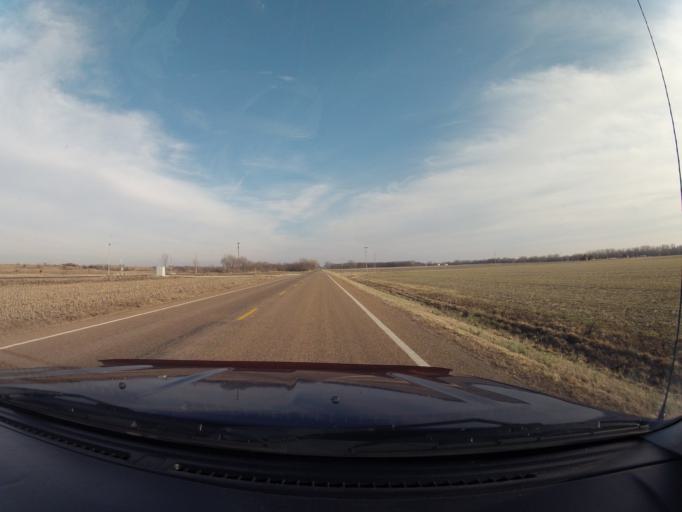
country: US
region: Kansas
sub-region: Pottawatomie County
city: Saint Marys
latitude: 39.2116
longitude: -96.1114
